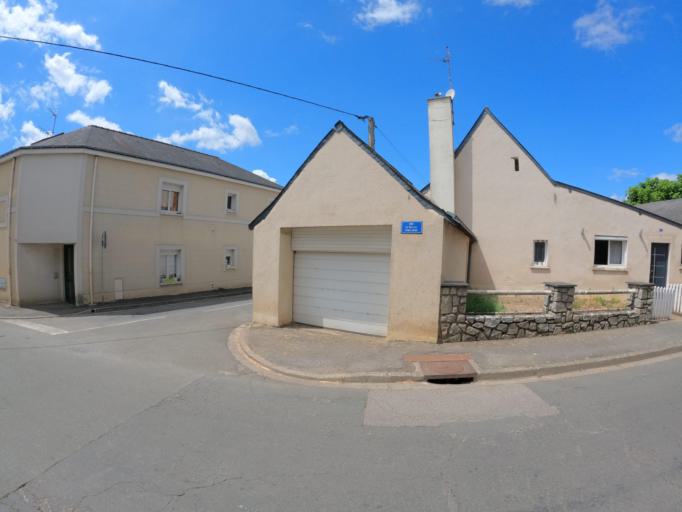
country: FR
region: Pays de la Loire
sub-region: Departement de Maine-et-Loire
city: Champigne
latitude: 47.6659
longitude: -0.5712
